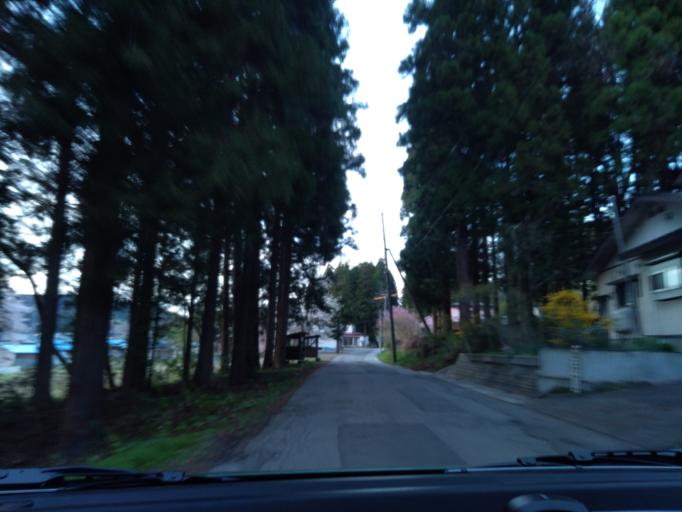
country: JP
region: Akita
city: Kakunodatemachi
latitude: 39.5865
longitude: 140.5760
